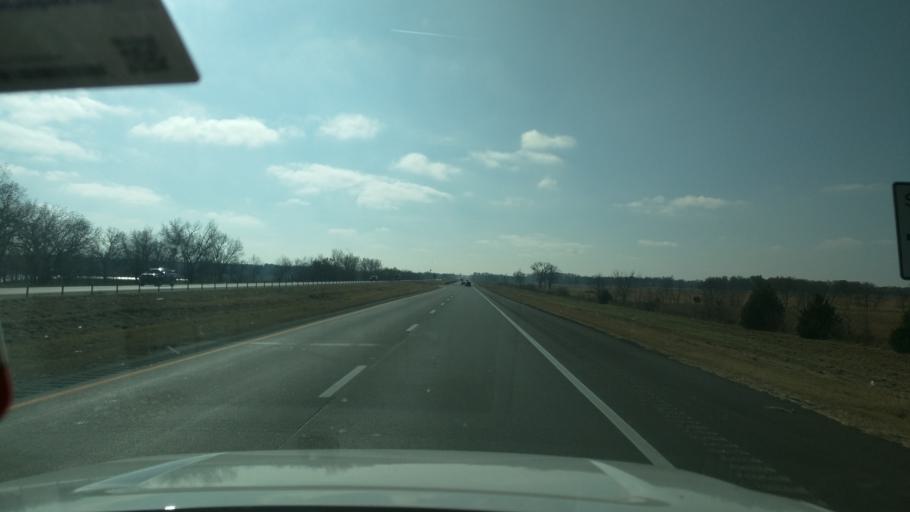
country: US
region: Oklahoma
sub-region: Washington County
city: Bartlesville
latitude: 36.6650
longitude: -95.9355
